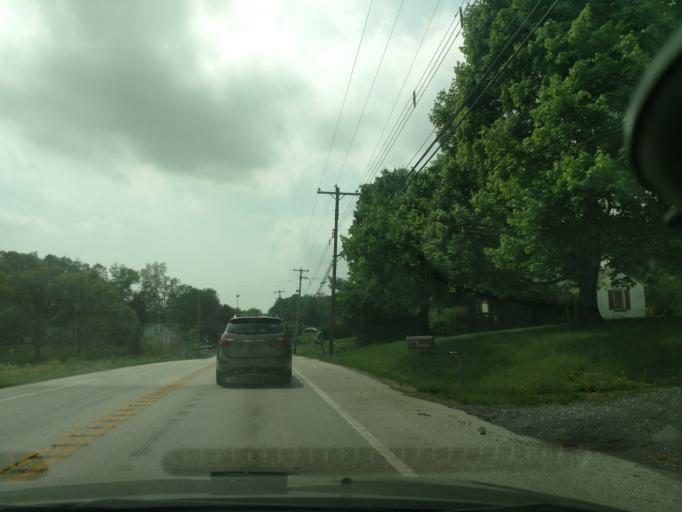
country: US
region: Pennsylvania
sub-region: Chester County
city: Kenilworth
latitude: 40.1748
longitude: -75.6647
